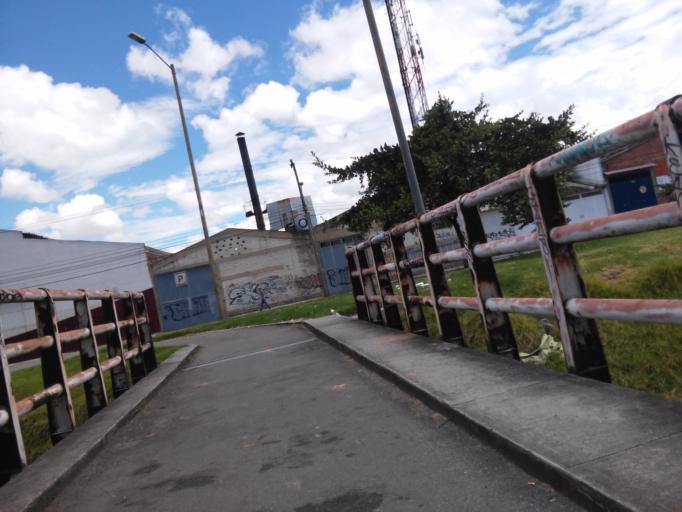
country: CO
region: Bogota D.C.
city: Bogota
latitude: 4.6122
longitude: -74.1039
